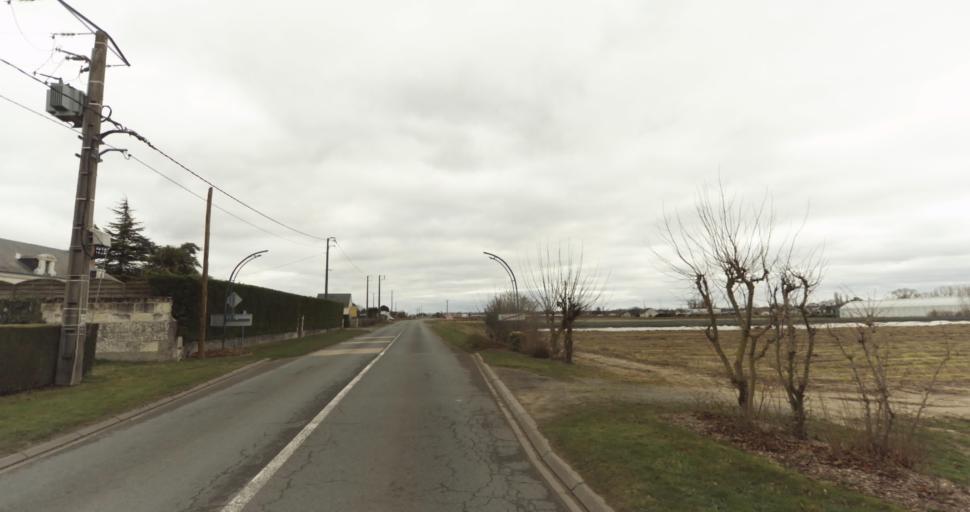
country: FR
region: Pays de la Loire
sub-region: Departement de Maine-et-Loire
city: Allonnes
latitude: 47.2914
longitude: 0.0326
